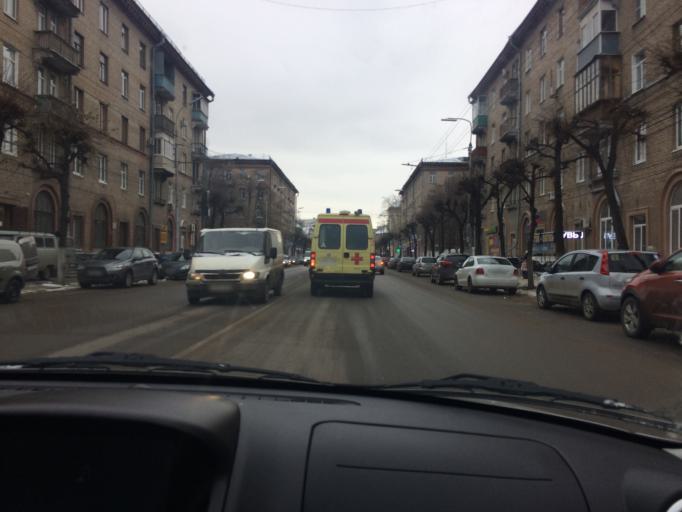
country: RU
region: Rjazan
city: Ryazan'
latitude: 54.6273
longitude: 39.7164
